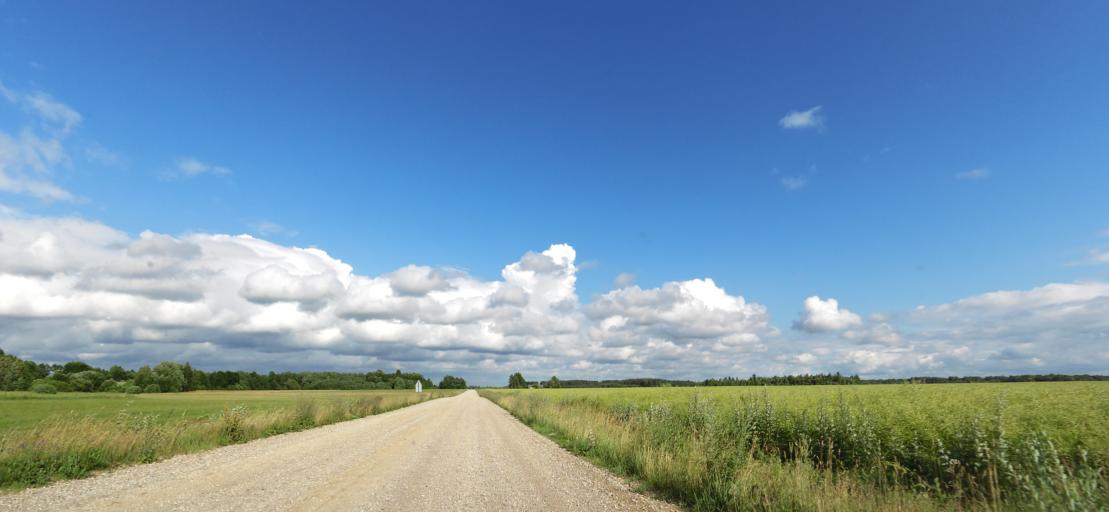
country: LT
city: Obeliai
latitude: 55.9144
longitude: 25.0696
